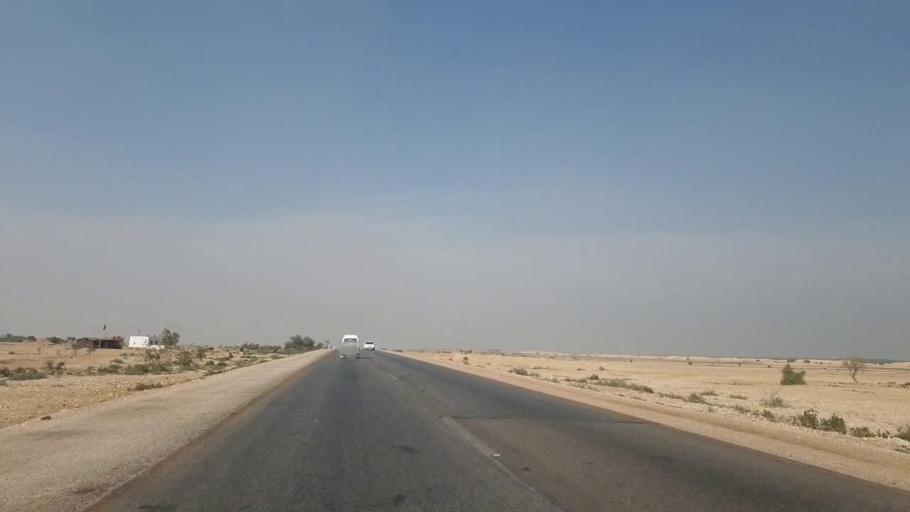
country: PK
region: Sindh
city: Hala
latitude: 25.8416
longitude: 68.2647
